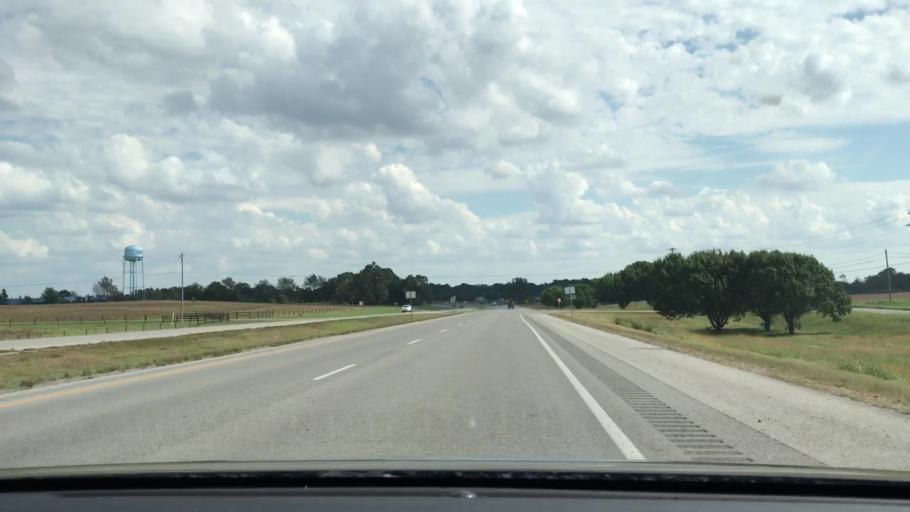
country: US
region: Kentucky
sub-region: Trigg County
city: Cadiz
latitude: 36.8674
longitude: -87.7852
